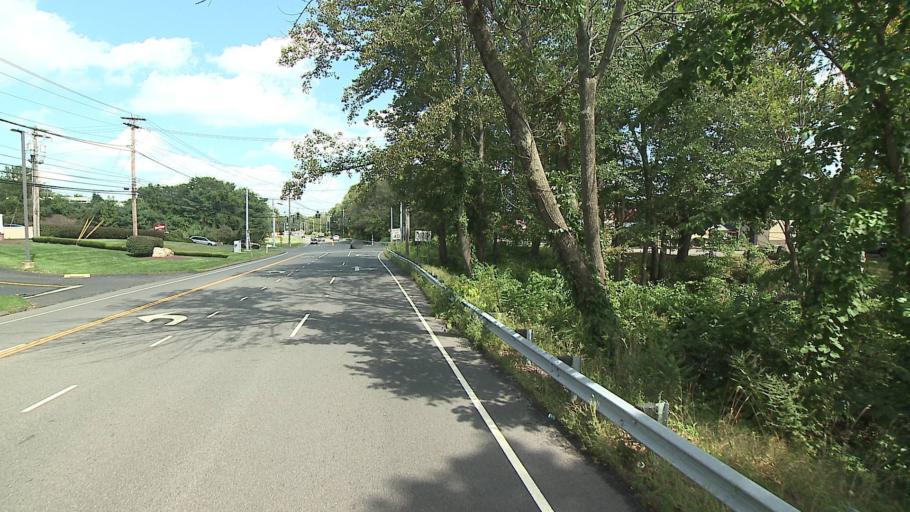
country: US
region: Connecticut
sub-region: Fairfield County
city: Shelton
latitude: 41.2632
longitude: -73.1349
